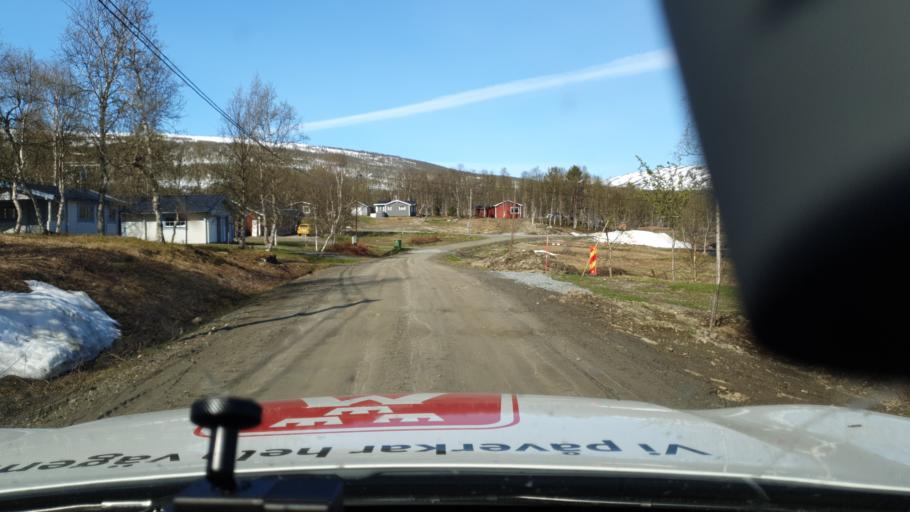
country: NO
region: Nordland
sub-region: Hattfjelldal
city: Hattfjelldal
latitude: 65.7119
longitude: 14.6171
